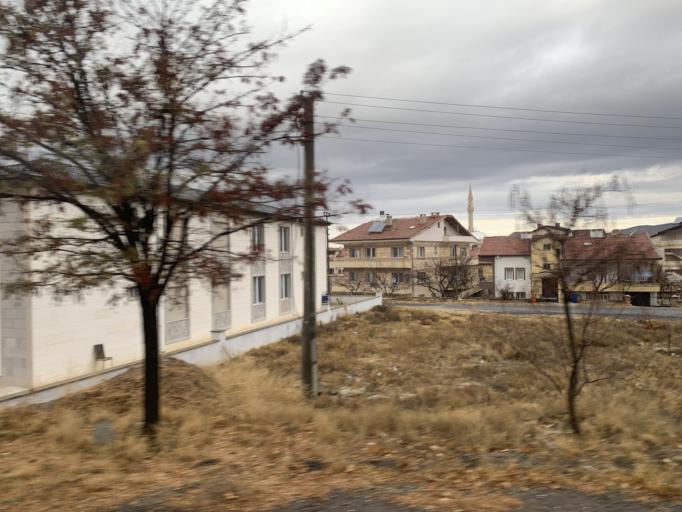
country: TR
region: Nevsehir
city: Avanos
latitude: 38.7066
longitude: 34.8573
